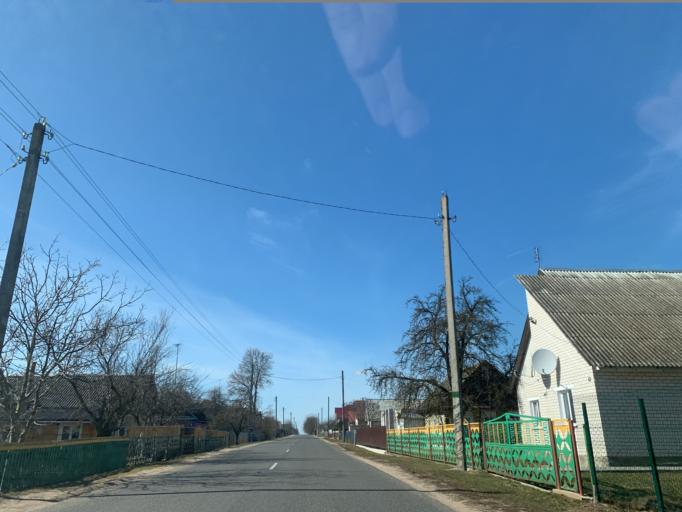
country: BY
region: Minsk
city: Haradzyeya
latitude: 53.3118
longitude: 26.5475
